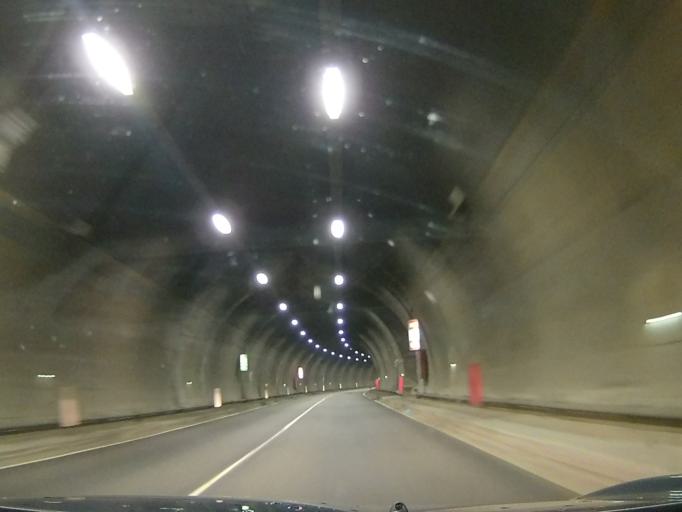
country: IT
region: Lombardy
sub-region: Provincia di Sondrio
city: Verceia
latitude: 46.1915
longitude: 9.4484
